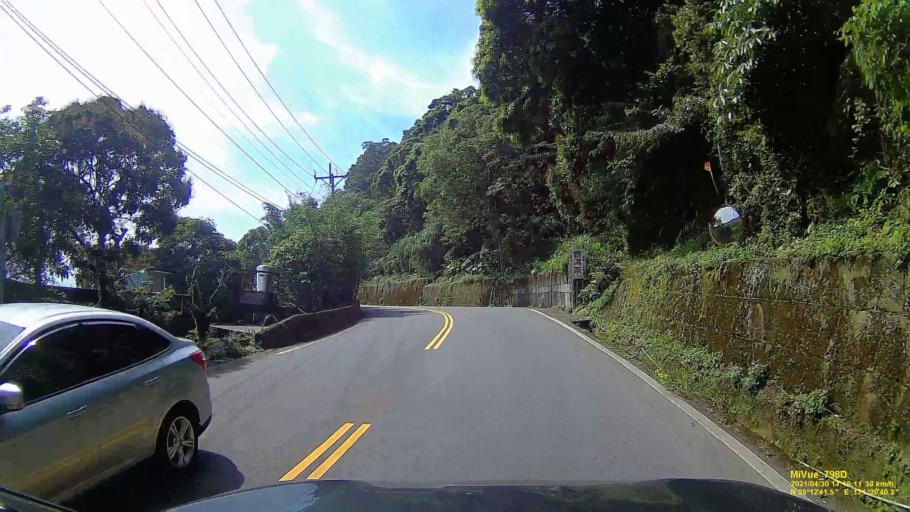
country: TW
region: Taipei
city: Taipei
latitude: 25.2115
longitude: 121.5111
